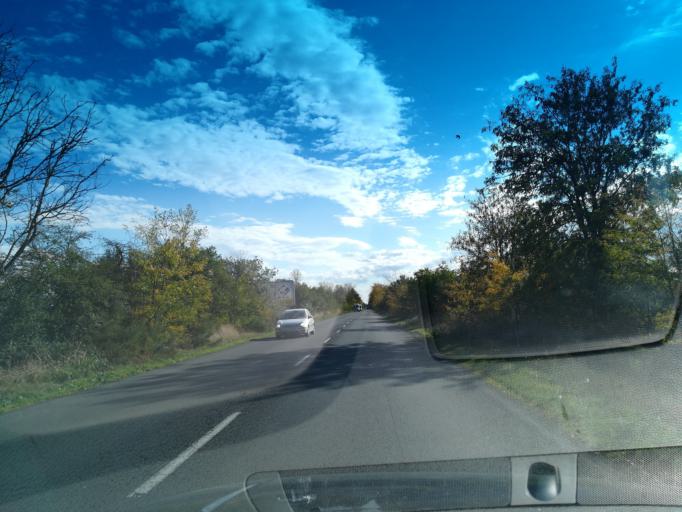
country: BG
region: Stara Zagora
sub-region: Obshtina Stara Zagora
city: Stara Zagora
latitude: 42.3798
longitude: 25.6505
